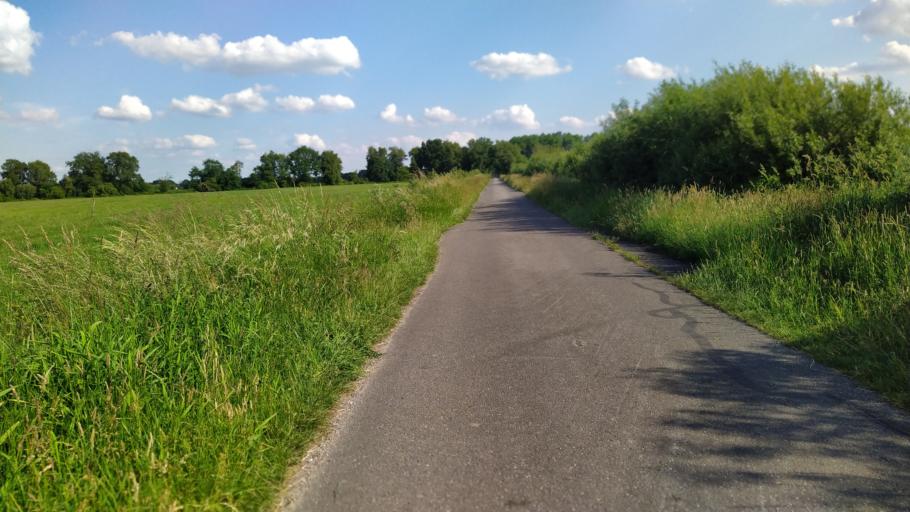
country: DE
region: Lower Saxony
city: Lintig
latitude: 53.6178
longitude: 8.8696
